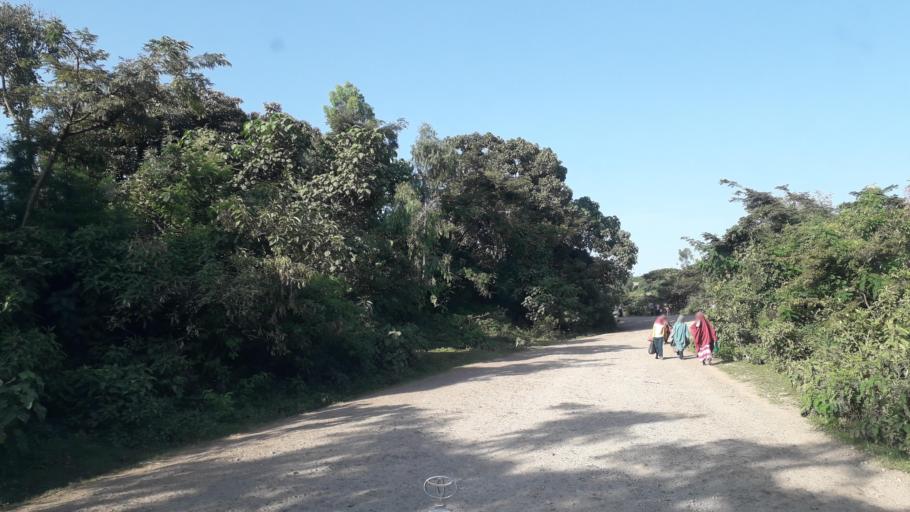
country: ET
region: Oromiya
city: Jima
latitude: 7.4850
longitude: 36.8789
